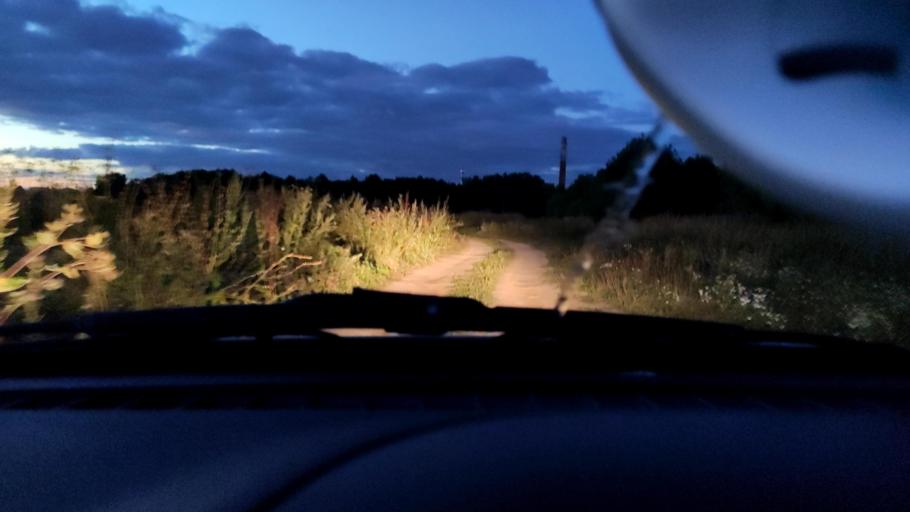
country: RU
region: Perm
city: Froly
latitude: 57.9444
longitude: 56.2535
